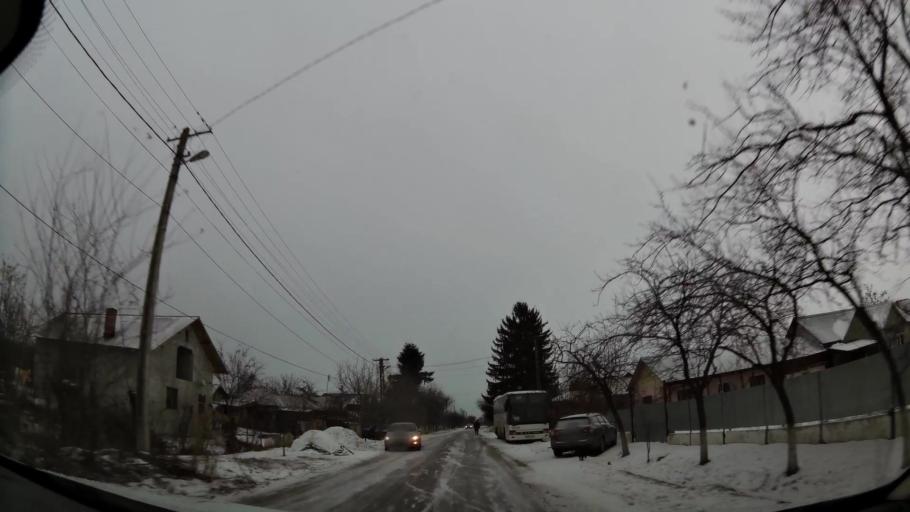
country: RO
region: Prahova
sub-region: Comuna Poenarii-Burchi
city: Ologeni
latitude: 44.7335
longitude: 25.9281
